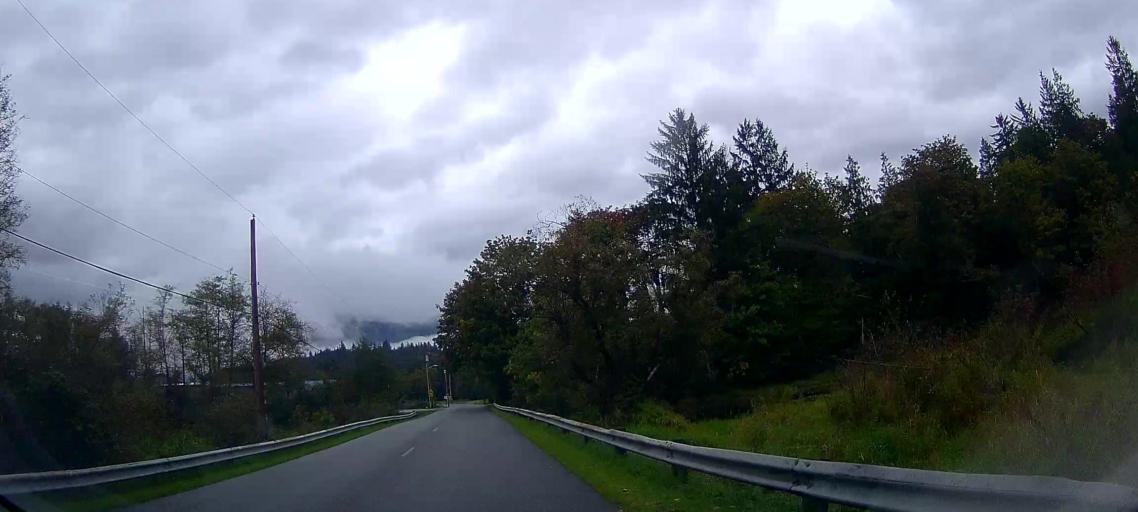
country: US
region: Washington
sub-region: Skagit County
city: Sedro-Woolley
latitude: 48.5269
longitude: -121.9900
